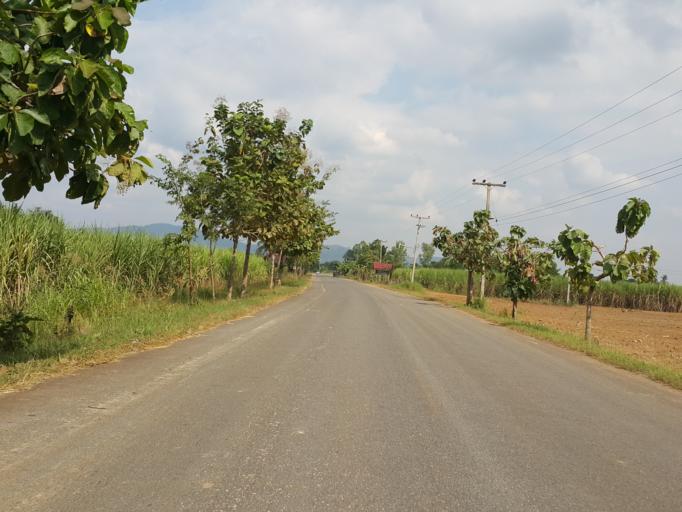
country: TH
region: Sukhothai
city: Thung Saliam
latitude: 17.4528
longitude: 99.6260
